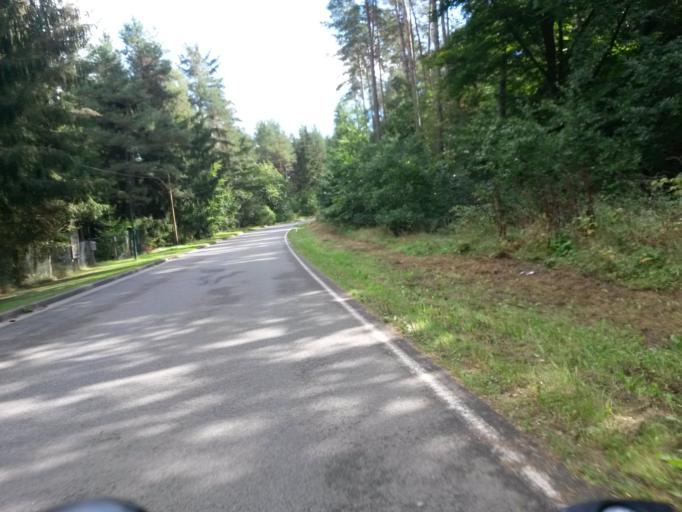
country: DE
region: Brandenburg
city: Templin
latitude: 53.2147
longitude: 13.5196
